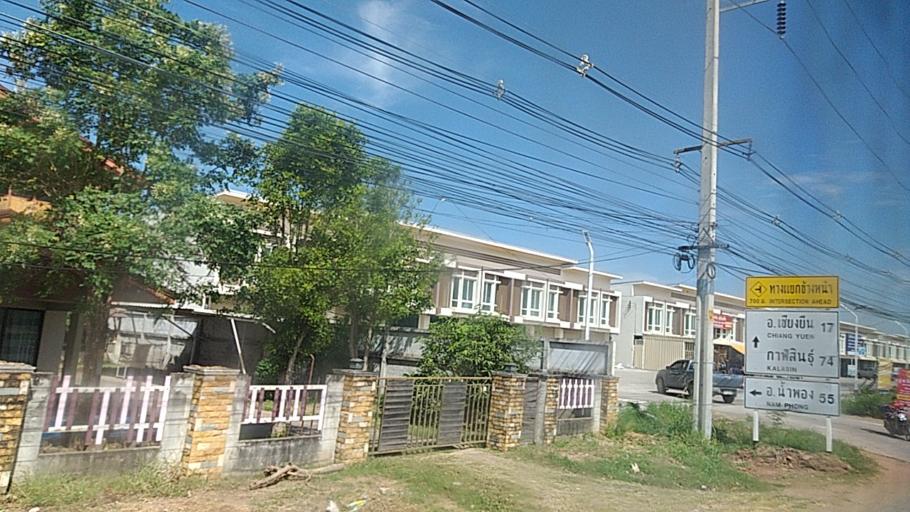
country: TH
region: Khon Kaen
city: Khon Kaen
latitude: 16.4436
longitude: 102.9465
